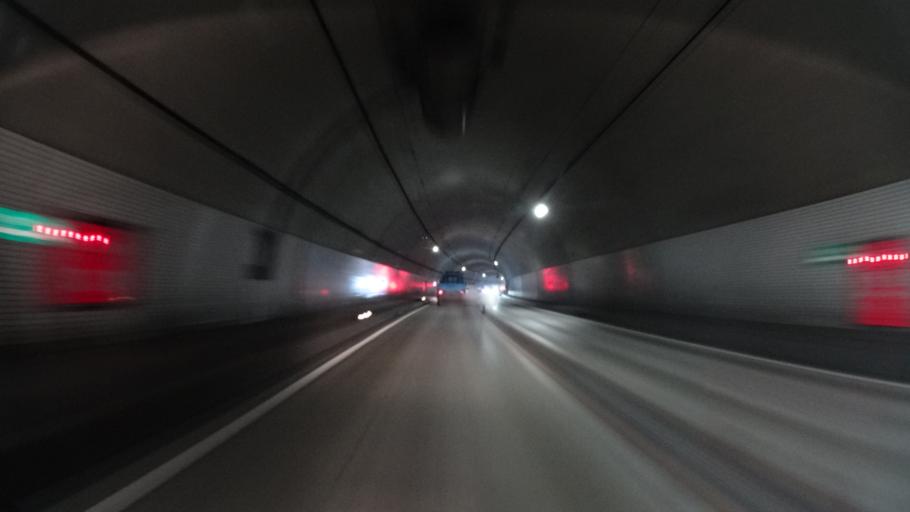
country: JP
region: Gunma
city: Numata
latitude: 36.6609
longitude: 139.1654
